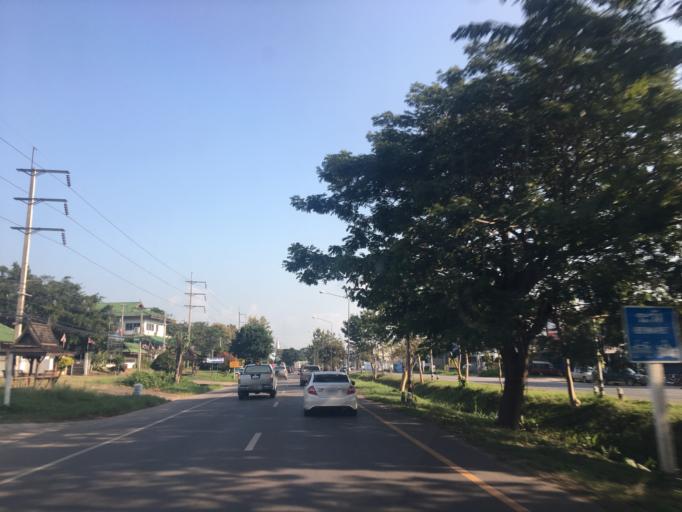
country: TH
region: Phayao
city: Phayao
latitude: 19.1675
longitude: 99.9096
